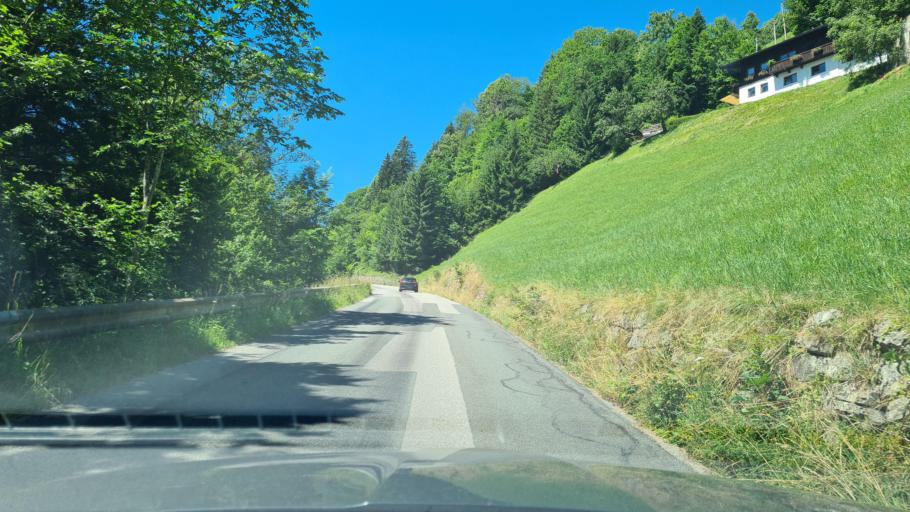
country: AT
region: Salzburg
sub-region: Politischer Bezirk Zell am See
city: Unken
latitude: 47.6484
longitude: 12.6993
